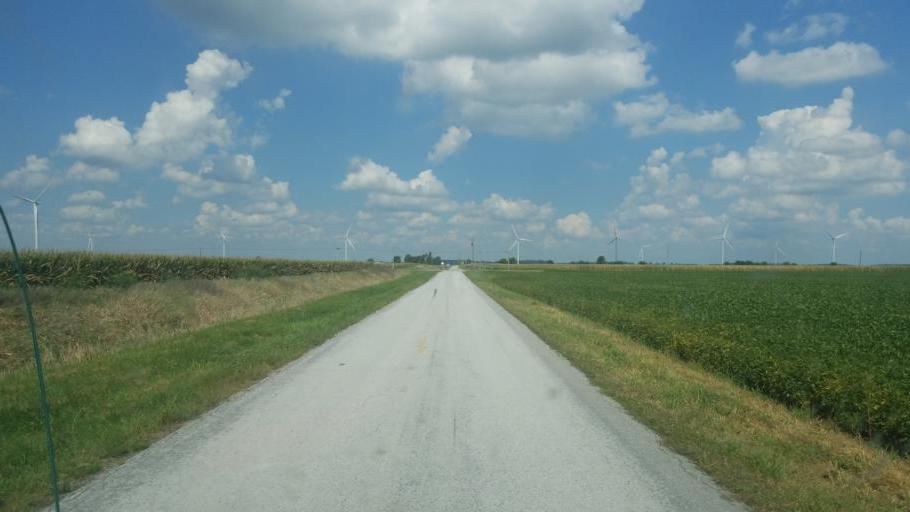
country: US
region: Ohio
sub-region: Hardin County
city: Ada
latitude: 40.7743
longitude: -83.7286
